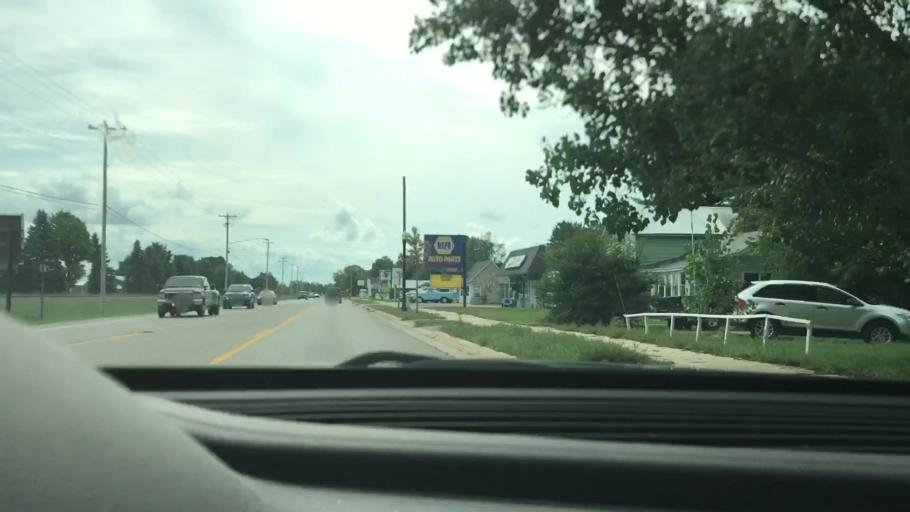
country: US
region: Michigan
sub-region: Antrim County
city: Mancelona
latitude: 44.8979
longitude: -85.0656
